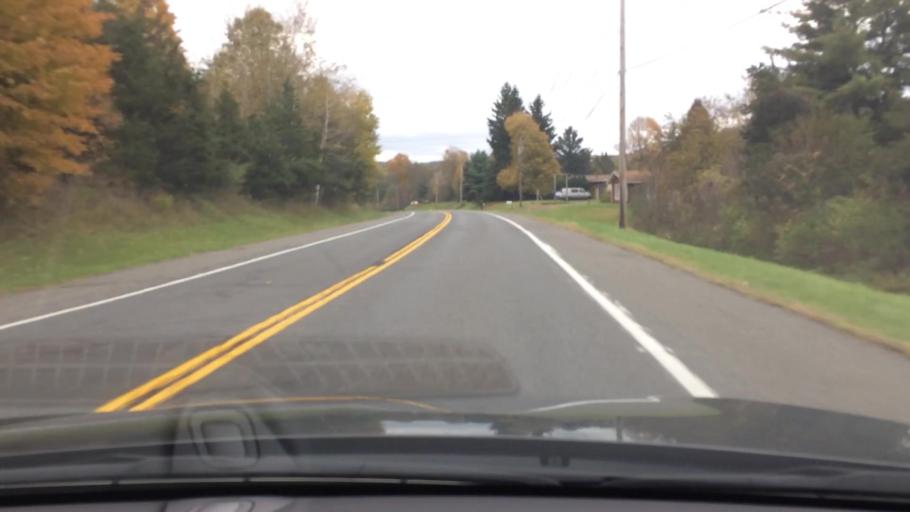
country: US
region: New York
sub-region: Columbia County
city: Oakdale
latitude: 42.1272
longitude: -73.7268
